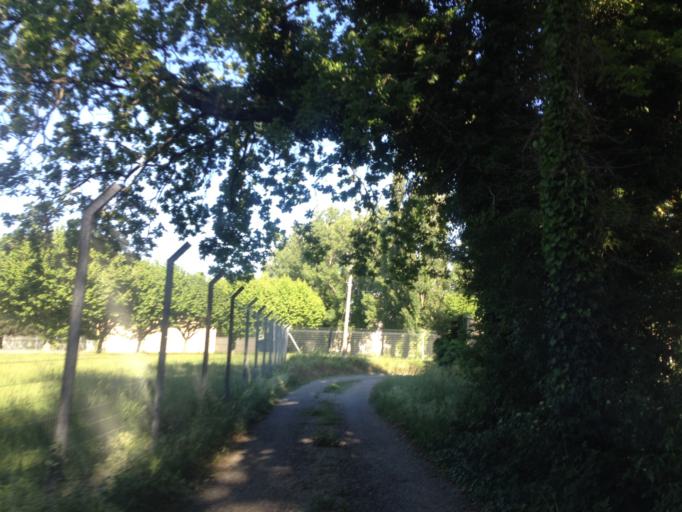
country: FR
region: Provence-Alpes-Cote d'Azur
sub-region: Departement du Vaucluse
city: Camaret-sur-Aigues
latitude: 44.1395
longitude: 4.8461
